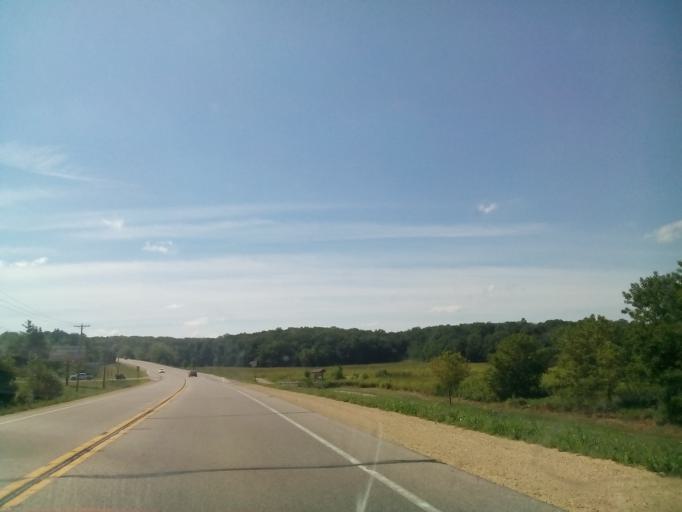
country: US
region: Wisconsin
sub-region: Green County
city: New Glarus
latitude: 42.7985
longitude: -89.6327
